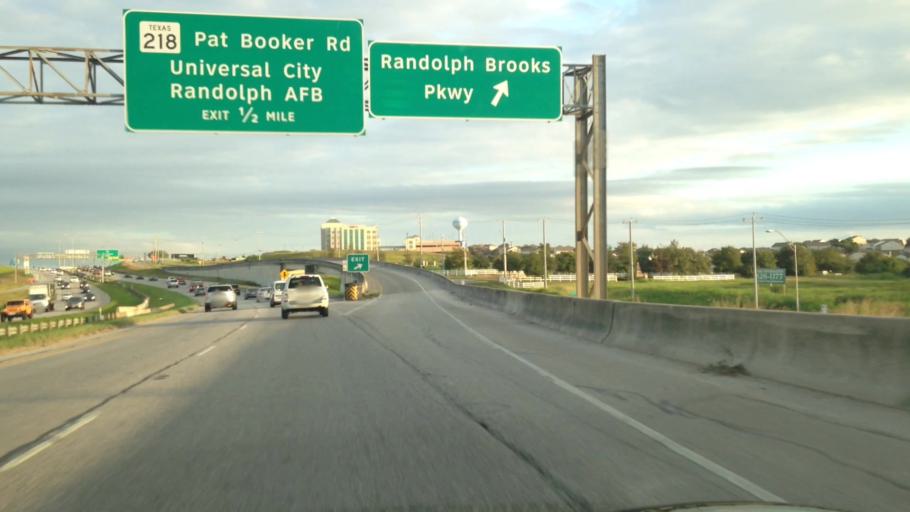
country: US
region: Texas
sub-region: Bexar County
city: Live Oak
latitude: 29.5779
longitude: -98.3425
